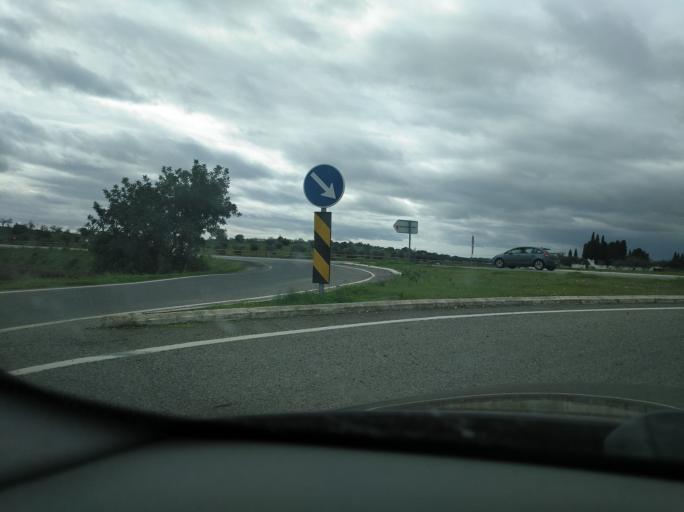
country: PT
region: Faro
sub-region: Castro Marim
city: Castro Marim
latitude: 37.2153
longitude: -7.4381
